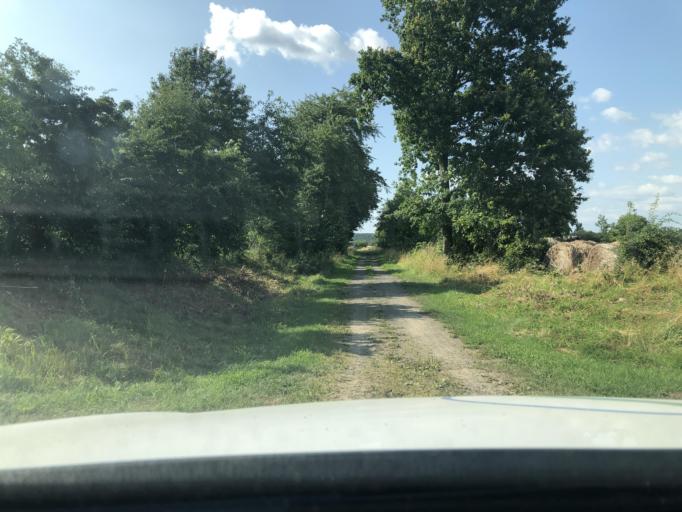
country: SE
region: Skane
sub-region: Kristianstads Kommun
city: Degeberga
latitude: 55.8178
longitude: 14.1238
